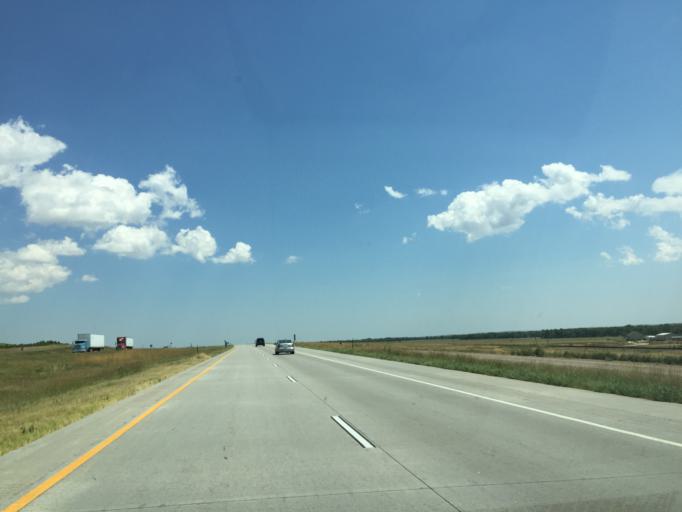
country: US
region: Colorado
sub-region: Lincoln County
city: Limon
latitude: 39.2818
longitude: -103.7726
